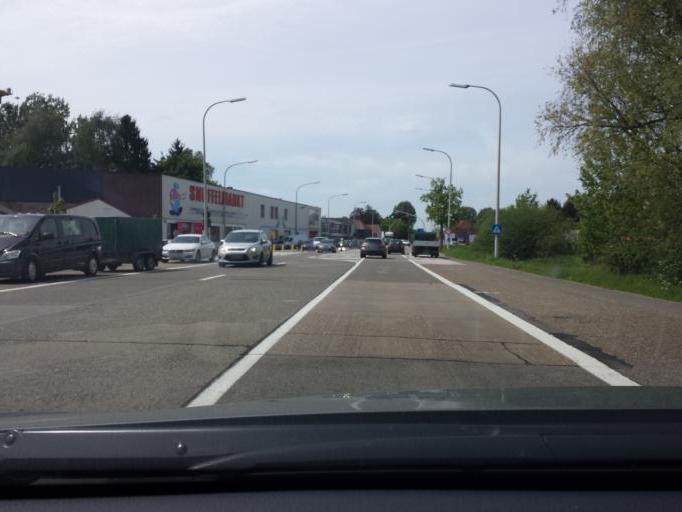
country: BE
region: Flanders
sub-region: Provincie Limburg
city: Halen
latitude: 50.9492
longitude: 5.1181
